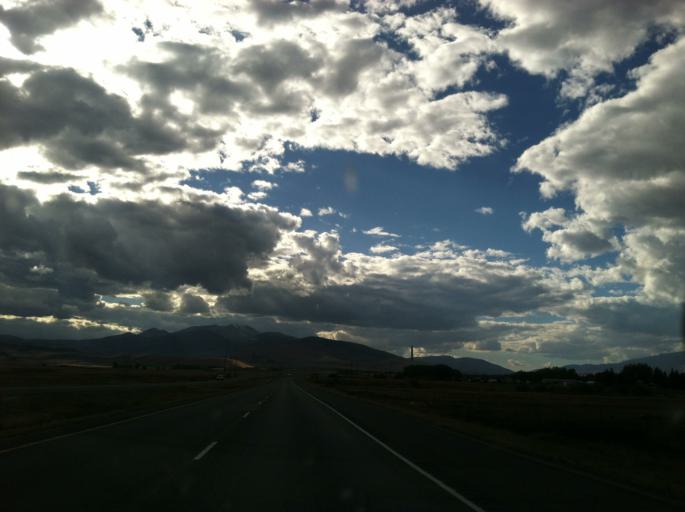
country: US
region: Montana
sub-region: Deer Lodge County
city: Warm Springs
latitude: 46.0958
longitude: -112.8169
